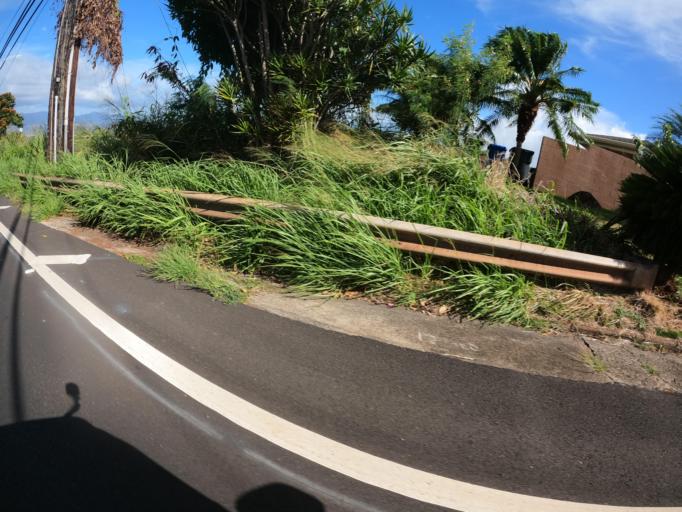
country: US
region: Hawaii
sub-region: Honolulu County
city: Halawa Heights
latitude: 21.3852
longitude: -157.9129
